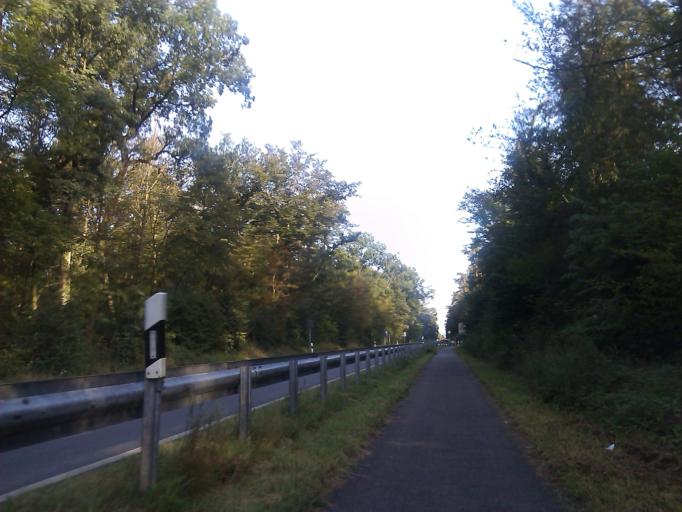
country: DE
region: Baden-Wuerttemberg
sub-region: Karlsruhe Region
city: Oftersheim
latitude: 49.3425
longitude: 8.6046
